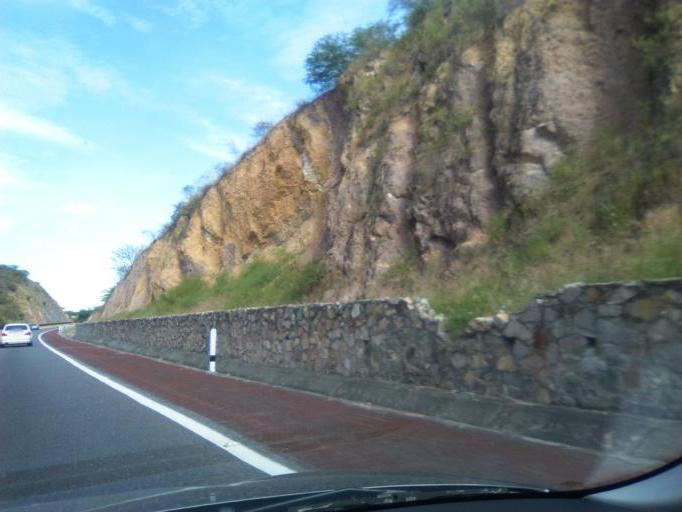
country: MX
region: Guerrero
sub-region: Huitzuco de los Figueroa
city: San Francisco Ozomatlan
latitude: 17.9721
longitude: -99.3358
